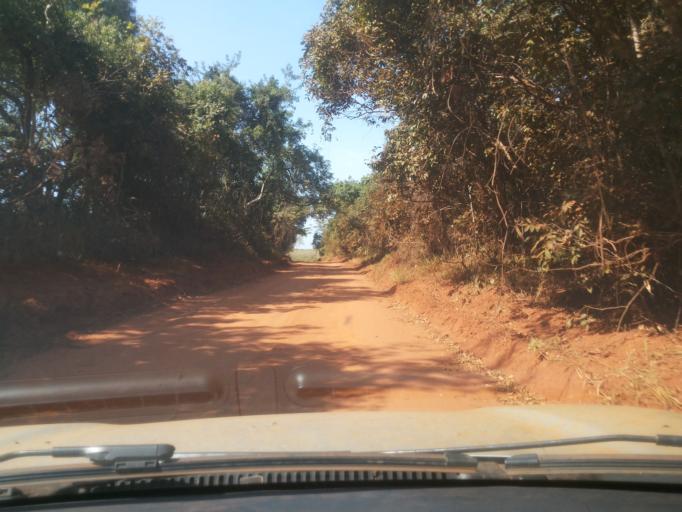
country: BR
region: Minas Gerais
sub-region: Ituiutaba
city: Ituiutaba
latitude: -19.0443
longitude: -49.3749
